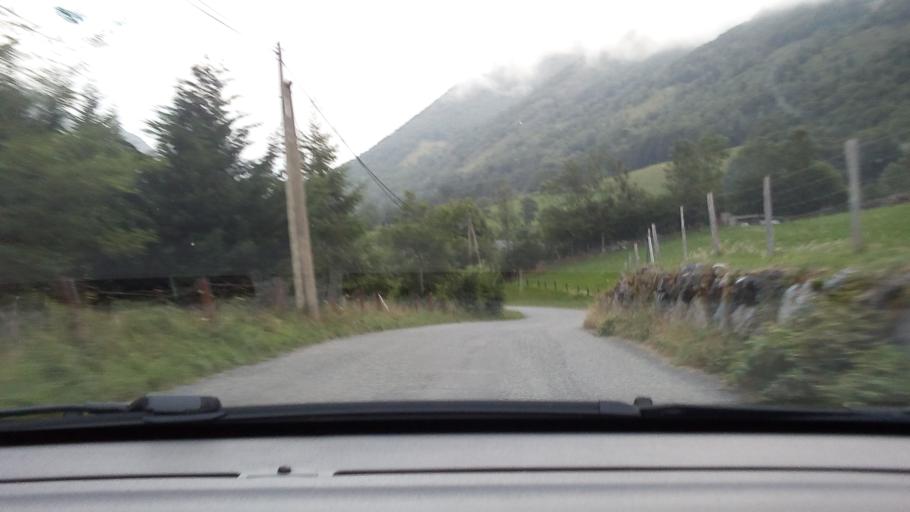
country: FR
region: Midi-Pyrenees
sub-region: Departement des Hautes-Pyrenees
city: Cauterets
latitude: 42.9199
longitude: -0.1864
